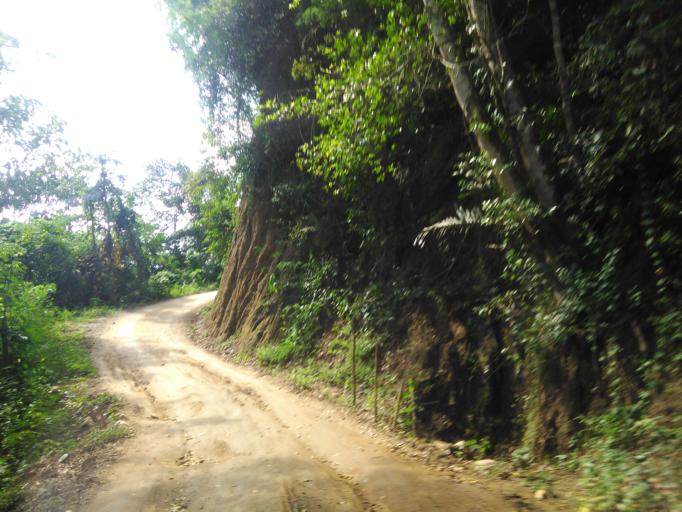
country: ID
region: South Sulawesi
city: Enrekang
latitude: -3.5145
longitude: 119.7337
